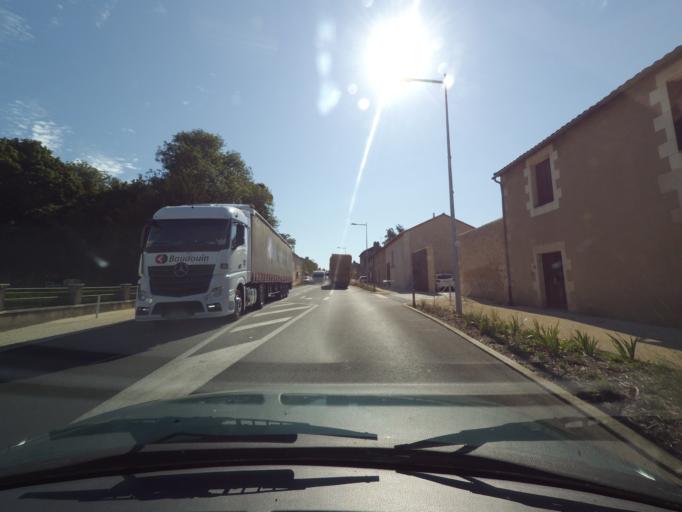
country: FR
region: Poitou-Charentes
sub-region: Departement de la Vienne
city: Lussac-les-Chateaux
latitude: 46.4034
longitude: 0.7202
